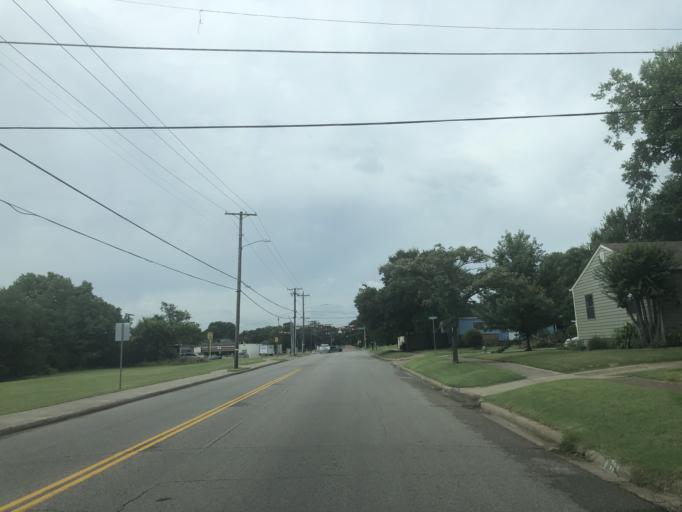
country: US
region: Texas
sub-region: Dallas County
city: Irving
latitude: 32.8024
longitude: -96.9469
